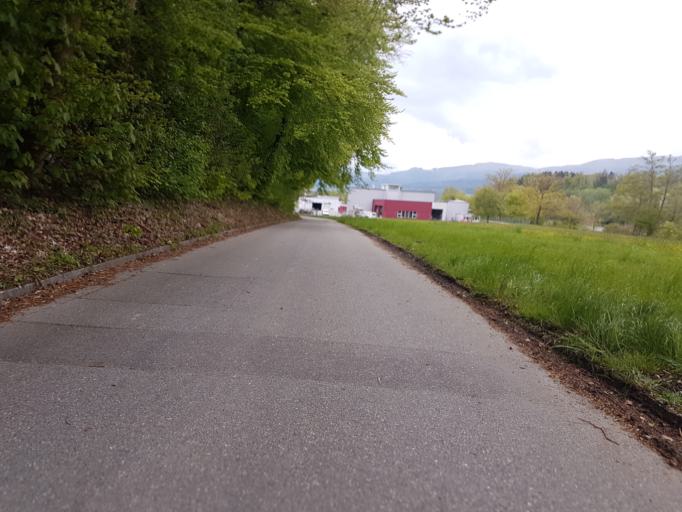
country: CH
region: Bern
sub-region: Oberaargau
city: Oberbipp
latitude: 47.2354
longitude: 7.6760
